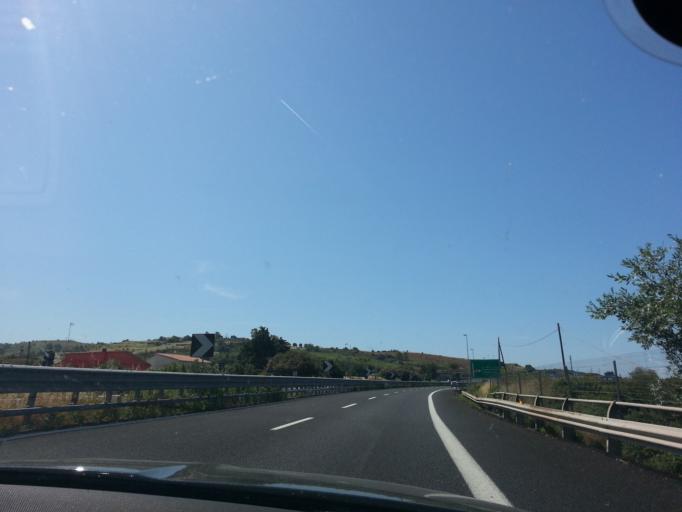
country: IT
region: Latium
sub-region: Citta metropolitana di Roma Capitale
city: Aurelia
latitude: 42.1262
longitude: 11.8237
